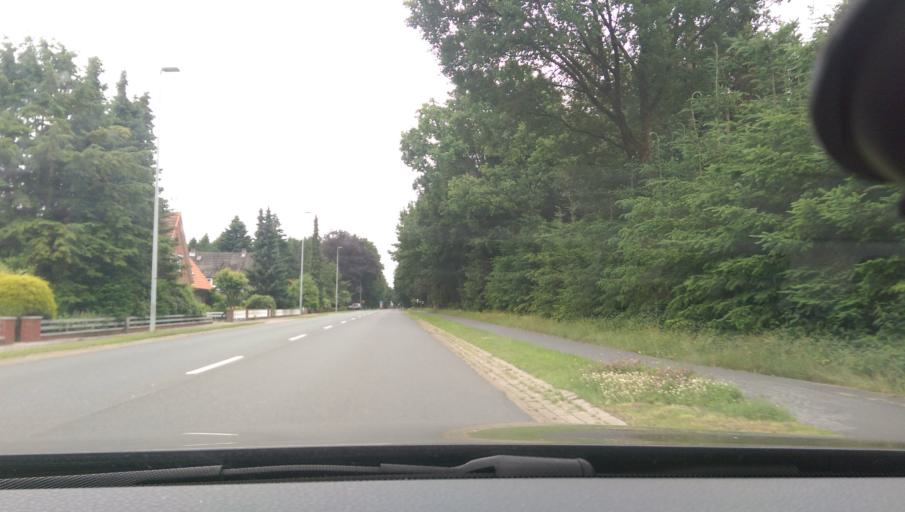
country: DE
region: Lower Saxony
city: Ahausen
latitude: 53.0762
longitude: 9.3545
